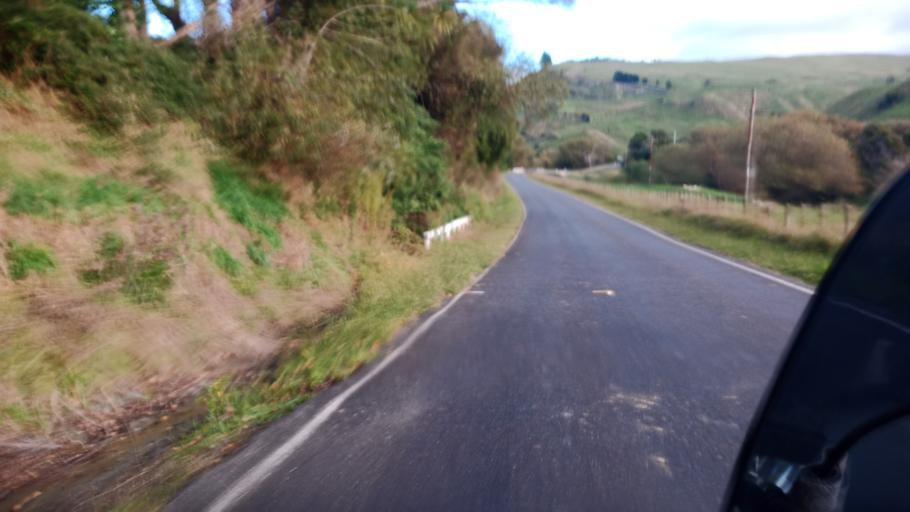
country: NZ
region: Gisborne
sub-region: Gisborne District
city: Gisborne
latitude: -38.5391
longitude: 177.5843
